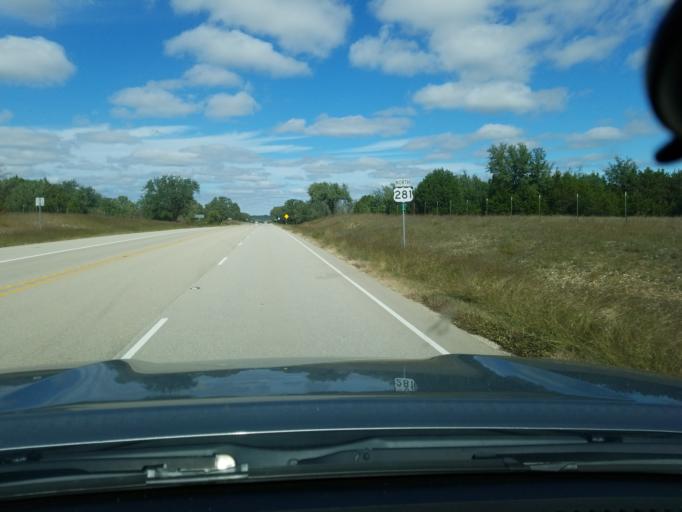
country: US
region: Texas
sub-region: Hamilton County
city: Hamilton
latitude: 31.5933
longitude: -98.1570
